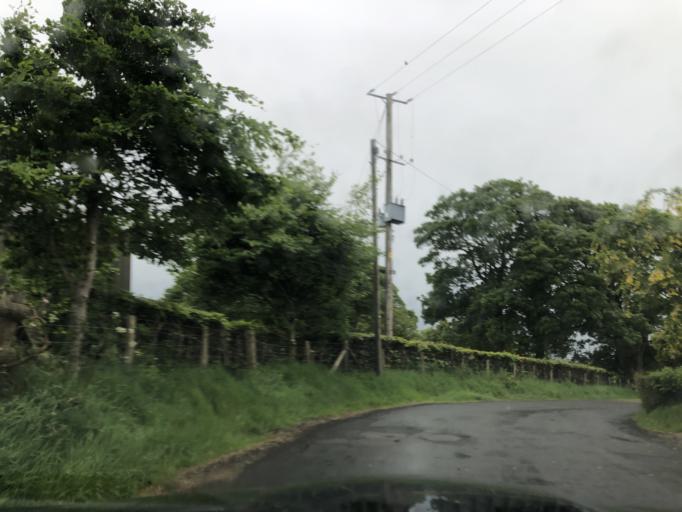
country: GB
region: Northern Ireland
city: Dunloy
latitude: 55.1368
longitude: -6.3728
